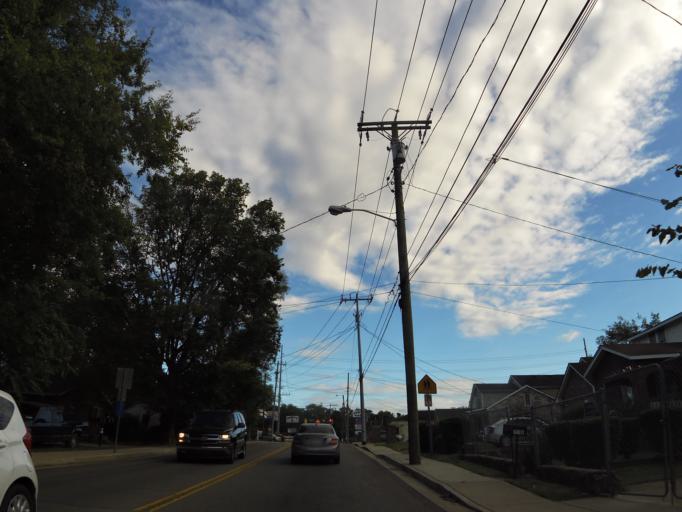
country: US
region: Tennessee
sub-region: Davidson County
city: Nashville
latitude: 36.1599
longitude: -86.8189
